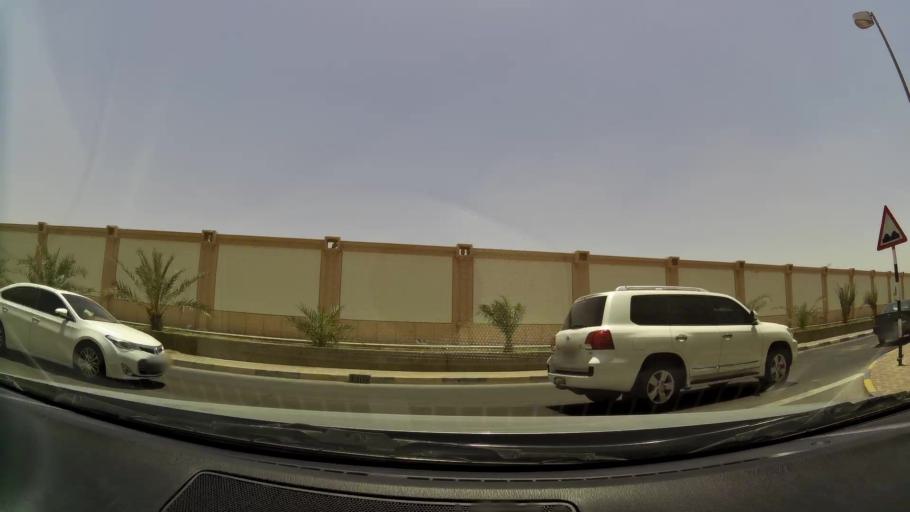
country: OM
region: Al Buraimi
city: Al Buraymi
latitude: 24.2757
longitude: 55.7367
